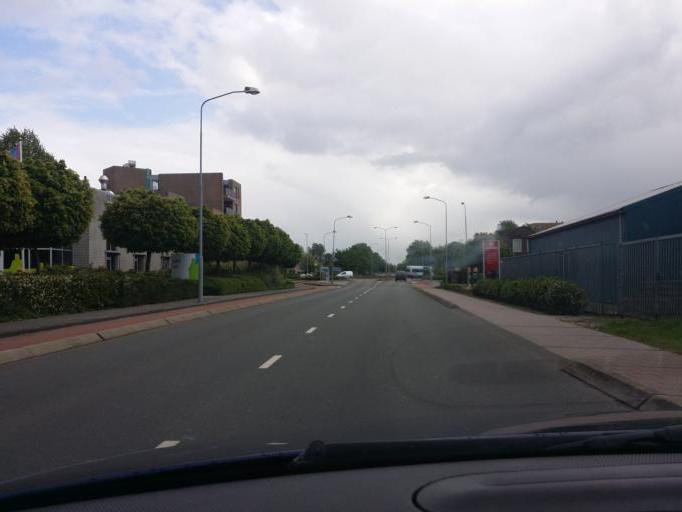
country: NL
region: Groningen
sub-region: Gemeente Hoogezand-Sappemeer
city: Hoogezand
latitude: 53.1641
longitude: 6.7391
